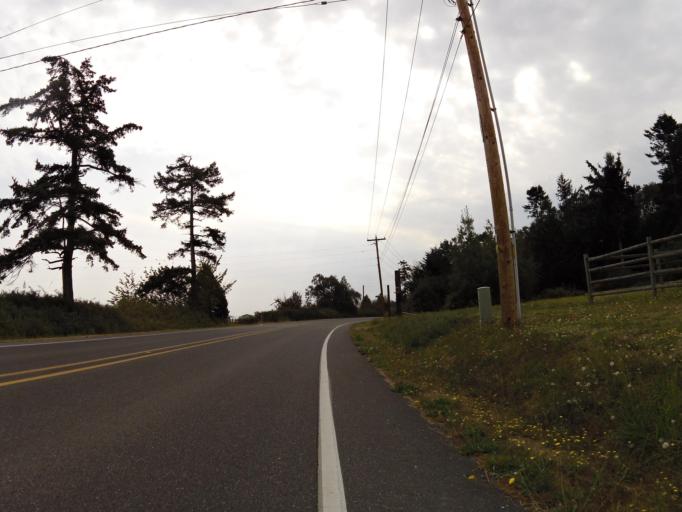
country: US
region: Washington
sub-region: Island County
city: Coupeville
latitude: 48.1887
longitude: -122.6679
